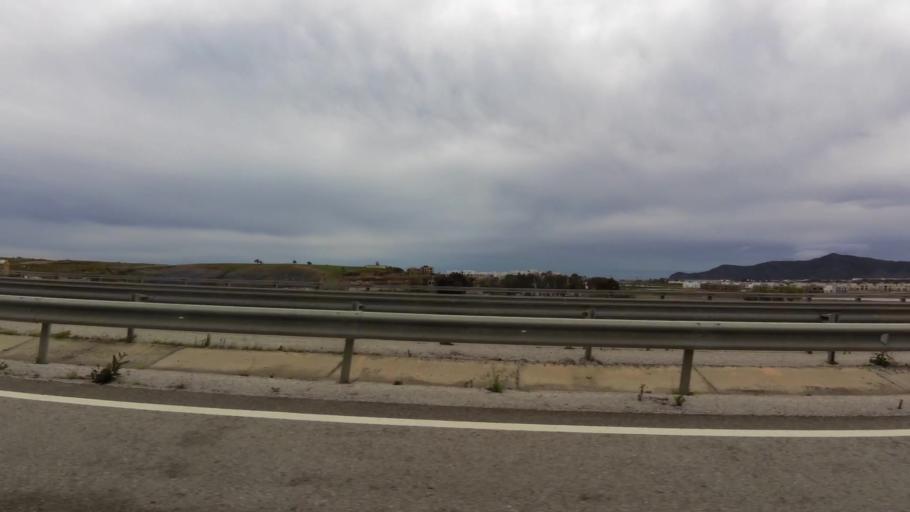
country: MA
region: Tanger-Tetouan
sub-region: Tetouan
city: Martil
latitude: 35.7208
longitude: -5.3532
